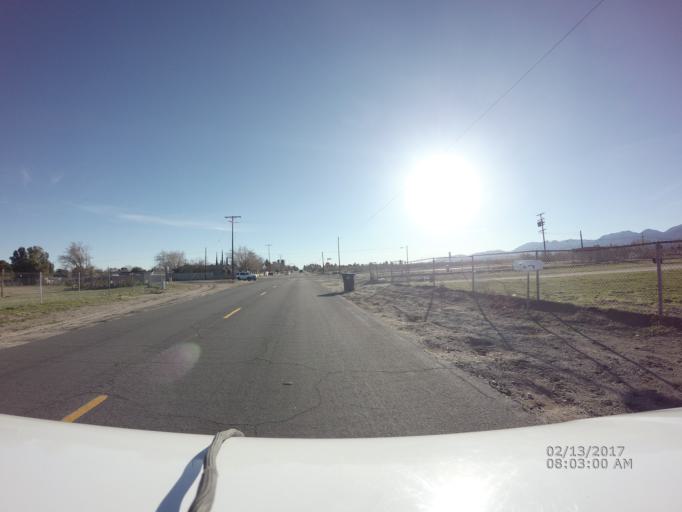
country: US
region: California
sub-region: Los Angeles County
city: Littlerock
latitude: 34.5284
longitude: -117.9756
